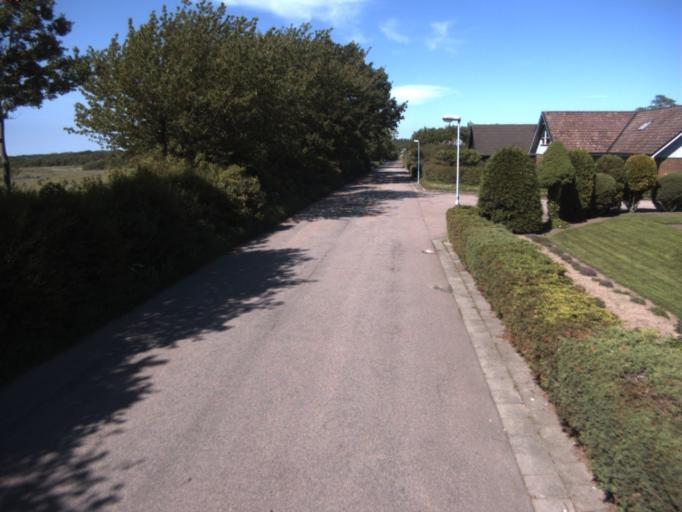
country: SE
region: Skane
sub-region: Helsingborg
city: Gantofta
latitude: 55.9872
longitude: 12.7946
